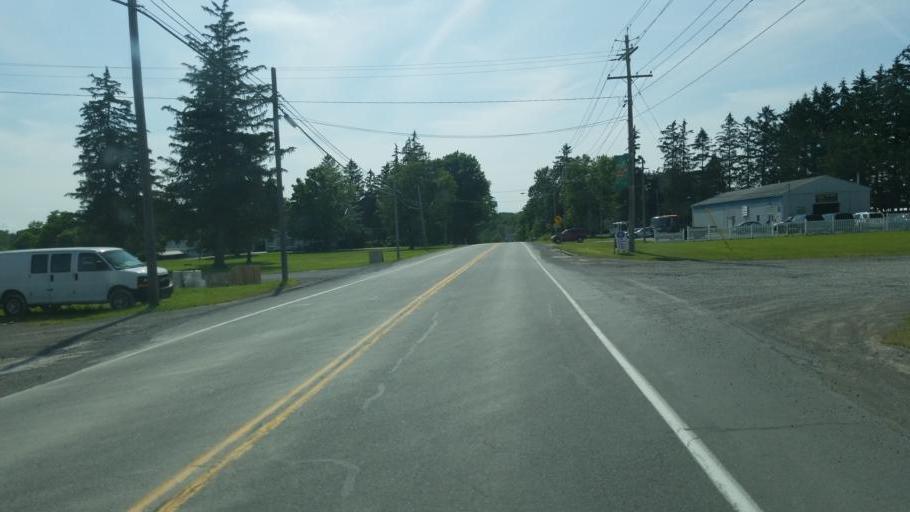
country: US
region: New York
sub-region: Livingston County
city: Lima
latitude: 42.9089
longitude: -77.5973
